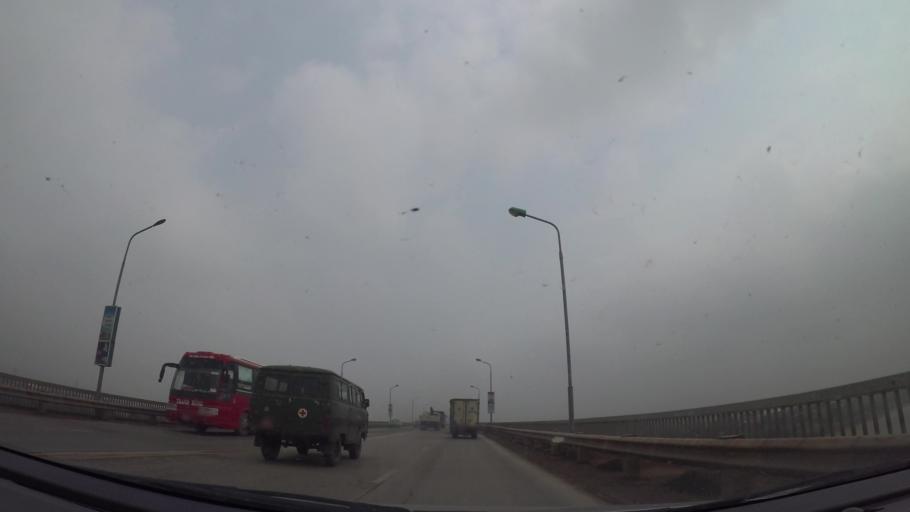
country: VN
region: Ha Noi
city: Tay Ho
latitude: 21.0995
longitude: 105.7865
